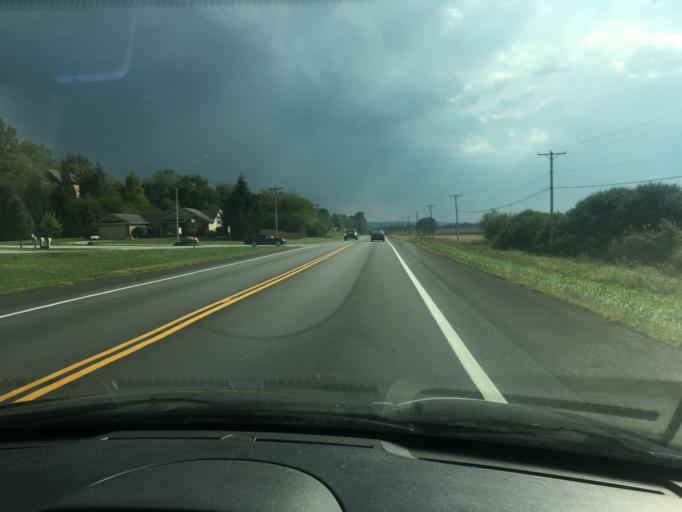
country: US
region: Ohio
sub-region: Champaign County
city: Urbana
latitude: 40.0604
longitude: -83.7777
